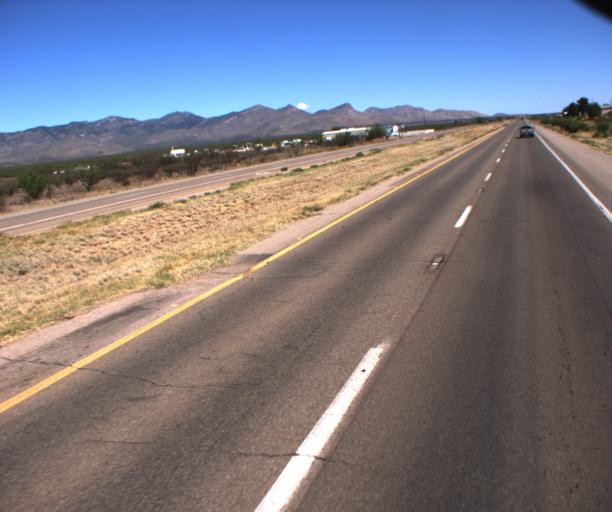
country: US
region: Arizona
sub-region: Cochise County
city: Huachuca City
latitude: 31.7089
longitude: -110.3502
